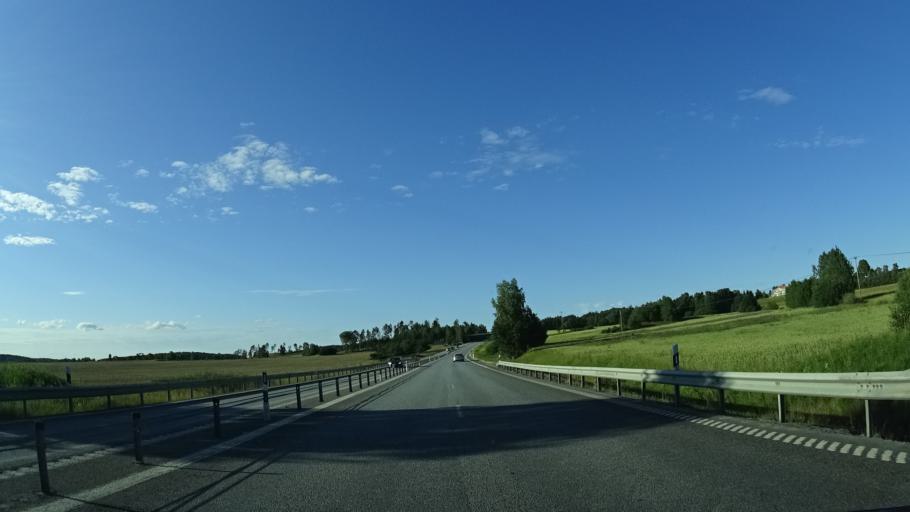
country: SE
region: Stockholm
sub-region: Osterakers Kommun
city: Akersberga
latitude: 59.5637
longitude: 18.2319
